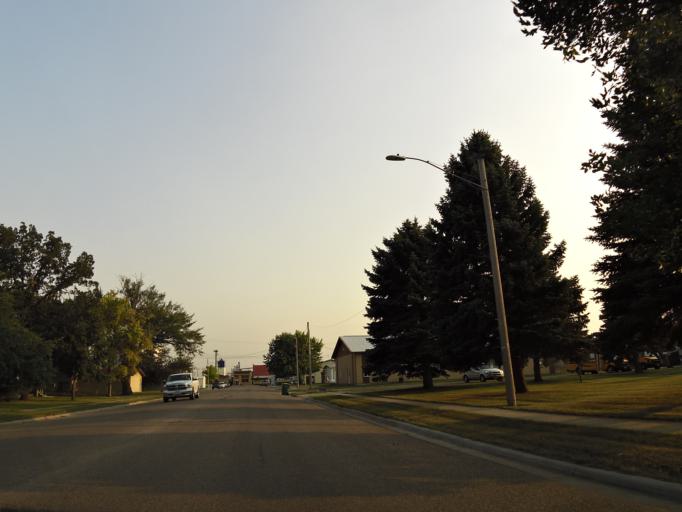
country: US
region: North Dakota
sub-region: Traill County
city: Mayville
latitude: 47.5004
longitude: -97.3710
